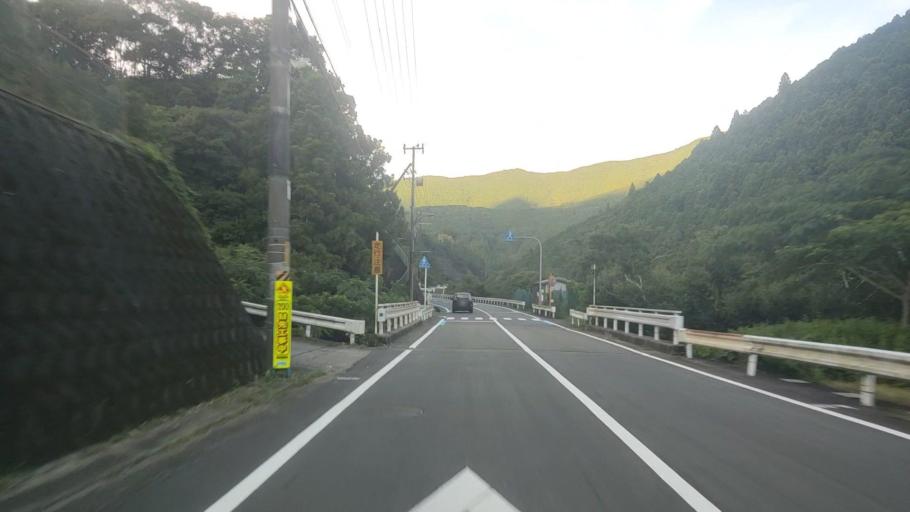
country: JP
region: Wakayama
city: Tanabe
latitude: 33.8107
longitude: 135.5413
